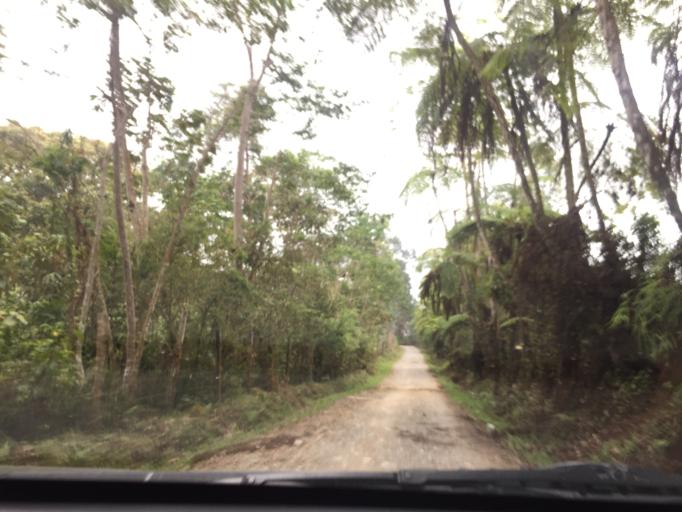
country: CO
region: Cundinamarca
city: Bojaca
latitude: 4.6878
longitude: -74.3734
